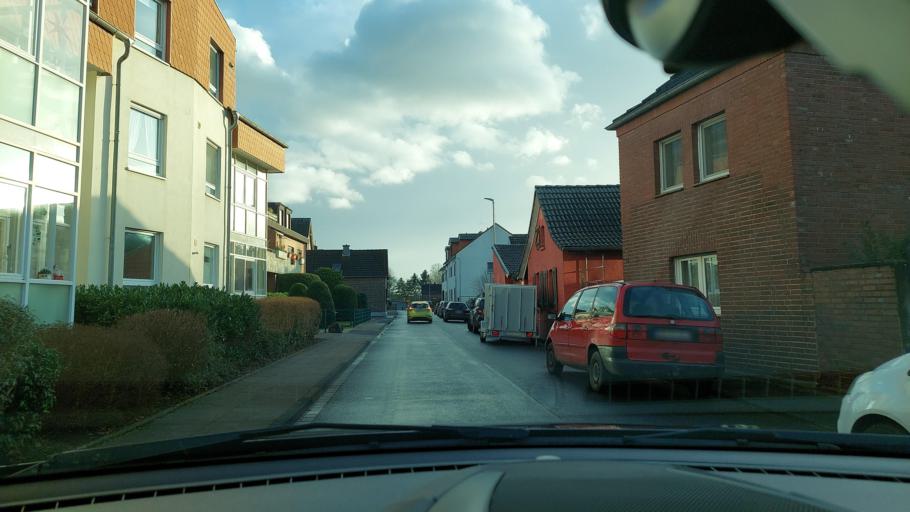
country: DE
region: North Rhine-Westphalia
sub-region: Regierungsbezirk Koln
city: Sinnersdorf
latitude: 51.0556
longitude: 6.8173
